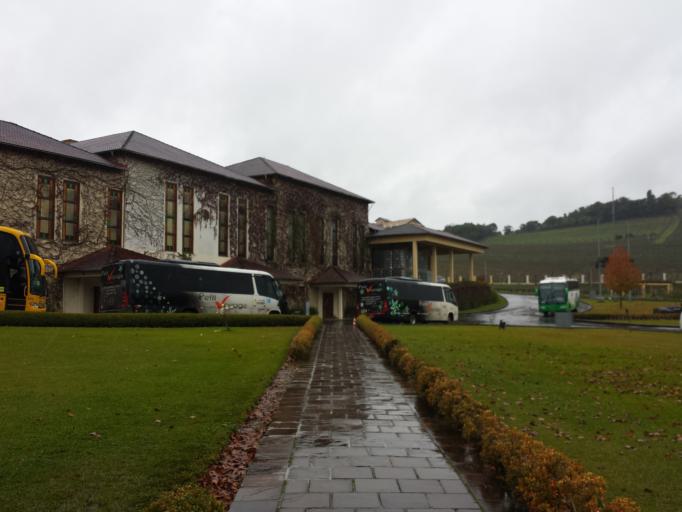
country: BR
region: Rio Grande do Sul
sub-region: Bento Goncalves
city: Bento Goncalves
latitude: -29.1830
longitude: -51.5833
